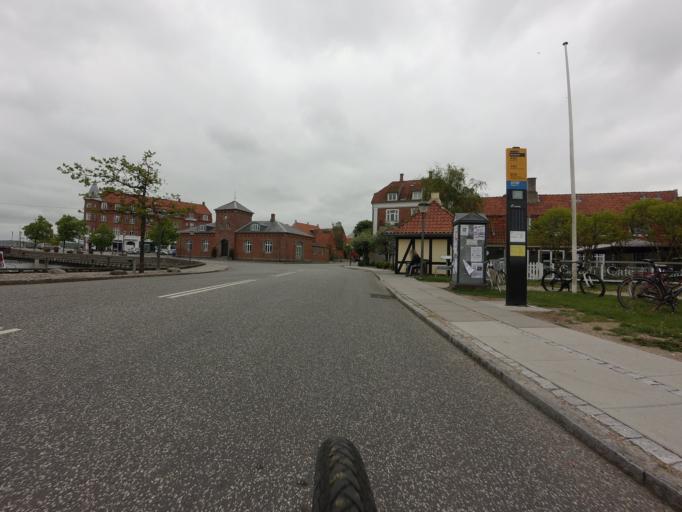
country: DK
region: Zealand
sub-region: Slagelse Kommune
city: Skaelskor
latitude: 55.2531
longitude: 11.2912
